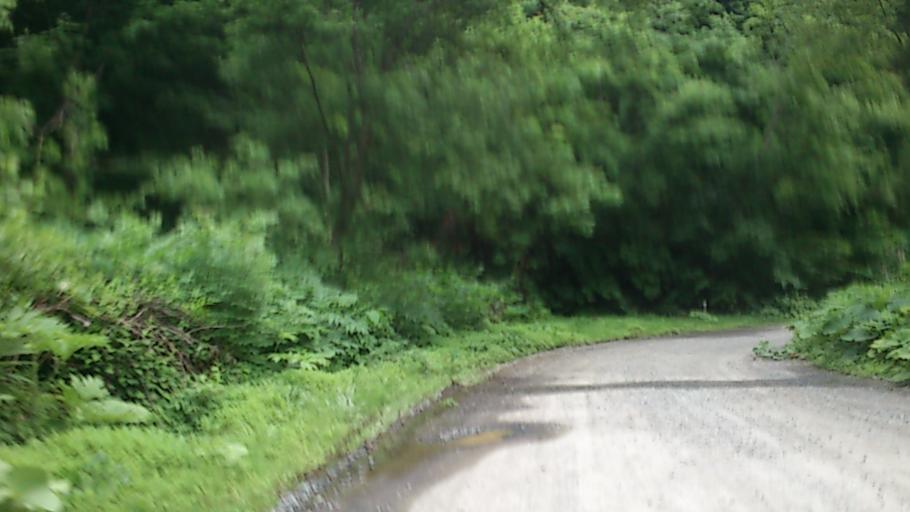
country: JP
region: Aomori
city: Hirosaki
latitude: 40.5439
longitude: 140.1799
